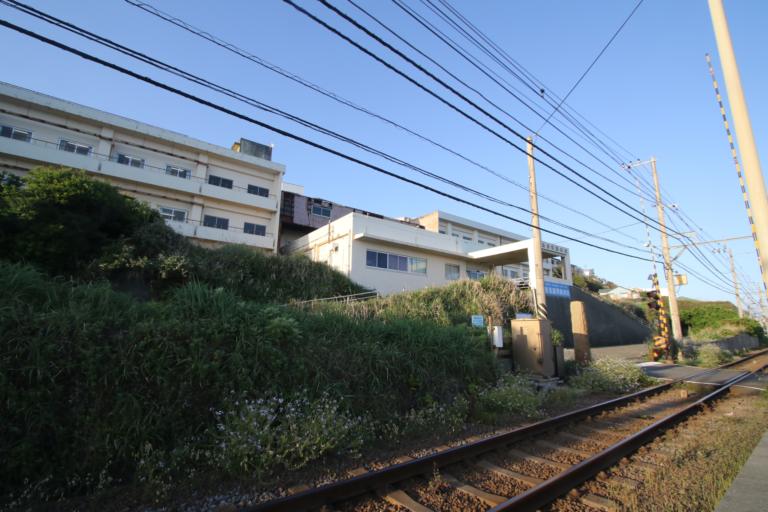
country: JP
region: Kanagawa
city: Fujisawa
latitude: 35.3067
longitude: 139.4978
